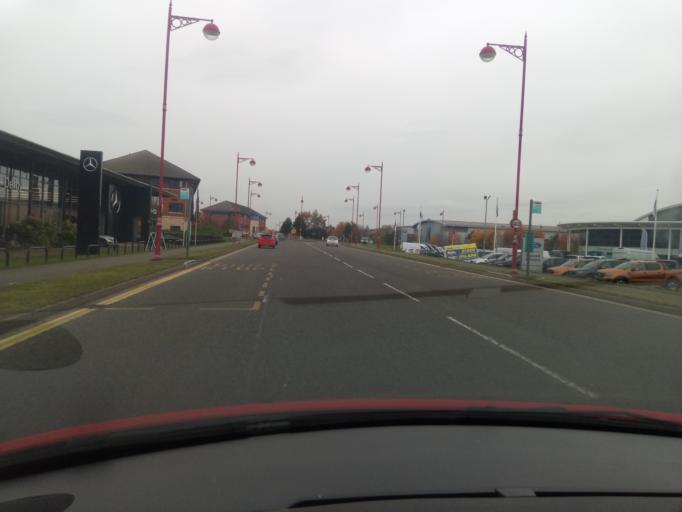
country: GB
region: England
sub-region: Derby
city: Derby
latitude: 52.9127
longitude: -1.4518
